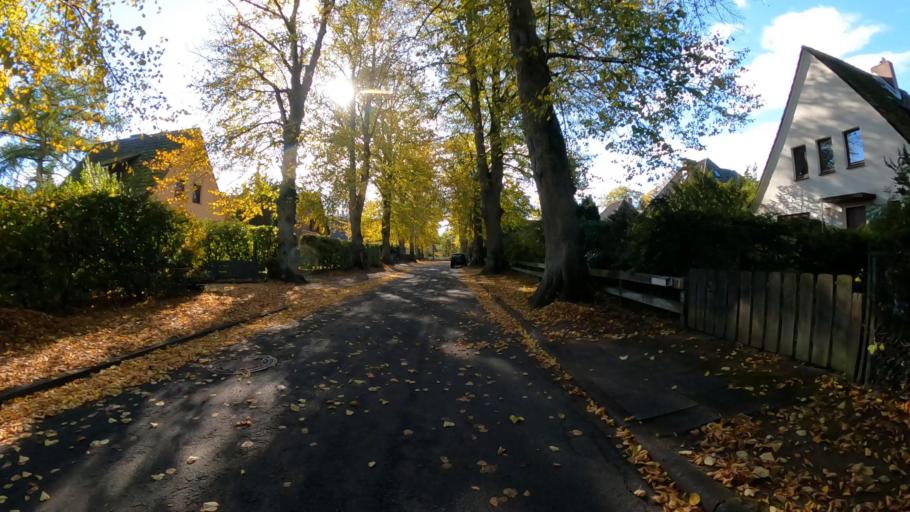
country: DE
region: Schleswig-Holstein
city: Ahrensburg
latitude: 53.6664
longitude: 10.2405
